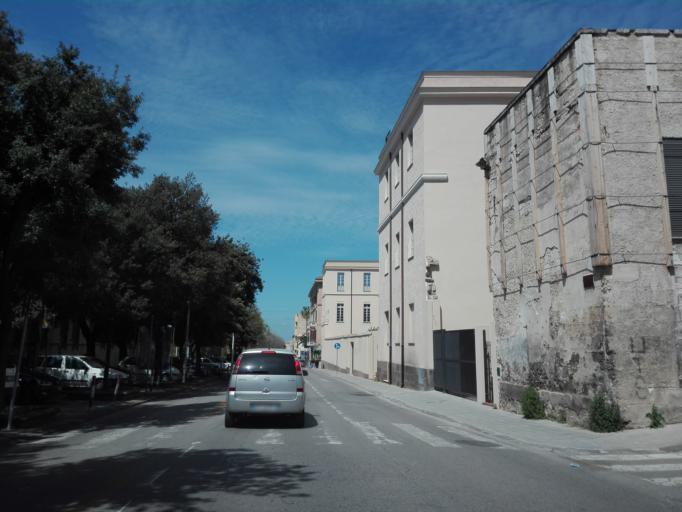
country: IT
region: Sardinia
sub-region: Provincia di Sassari
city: Sassari
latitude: 40.7221
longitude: 8.5630
